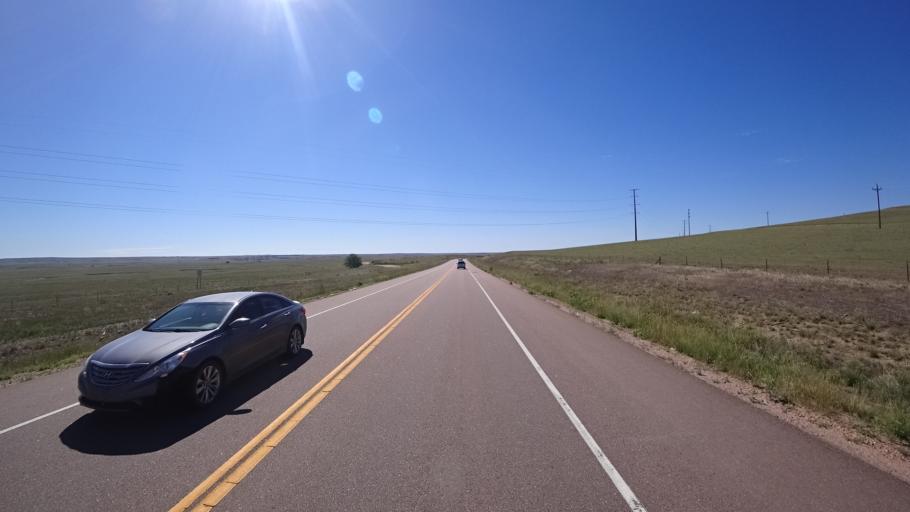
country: US
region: Colorado
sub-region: El Paso County
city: Cimarron Hills
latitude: 38.8044
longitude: -104.6655
